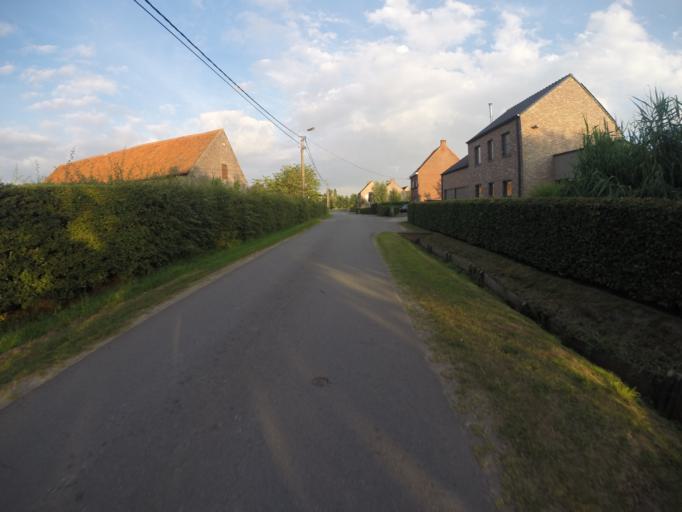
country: BE
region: Flanders
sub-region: Provincie West-Vlaanderen
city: Beernem
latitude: 51.1471
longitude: 3.3099
